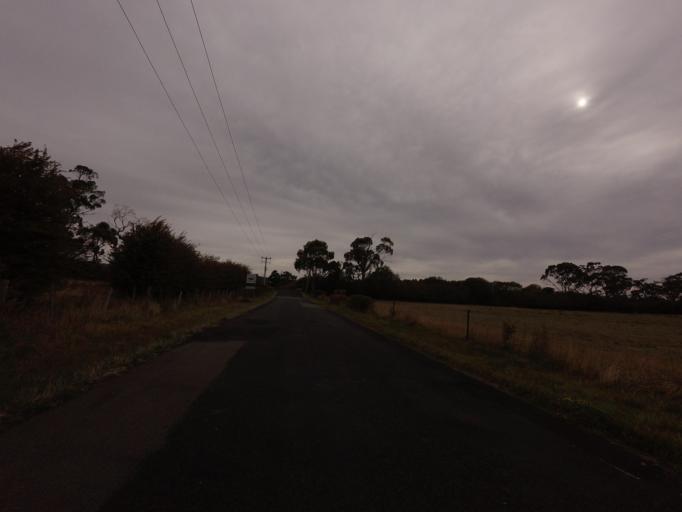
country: AU
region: Tasmania
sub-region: Sorell
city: Sorell
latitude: -42.6409
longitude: 147.5613
